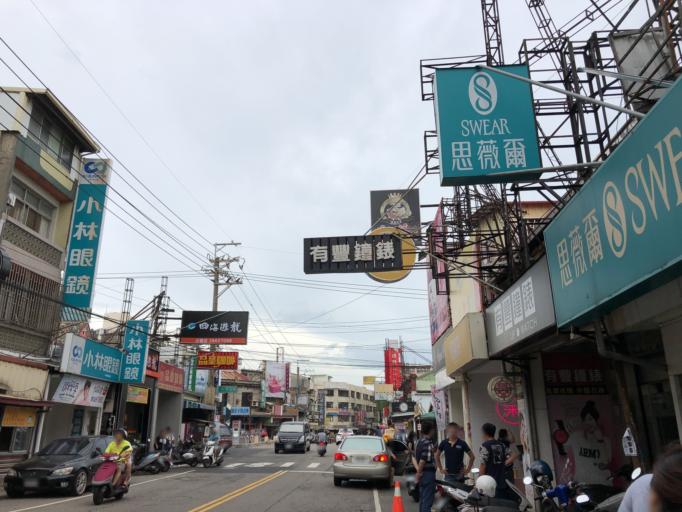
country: TW
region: Taiwan
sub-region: Taichung City
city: Taichung
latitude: 24.2377
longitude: 120.5615
